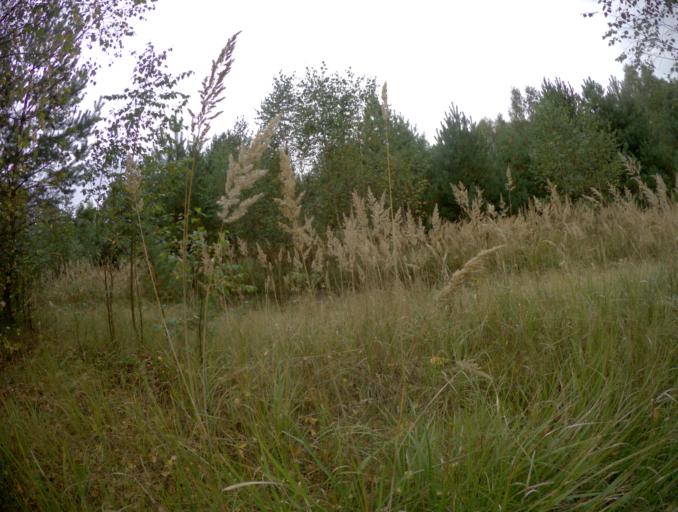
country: RU
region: Vladimir
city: Urshel'skiy
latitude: 55.8542
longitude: 40.2086
